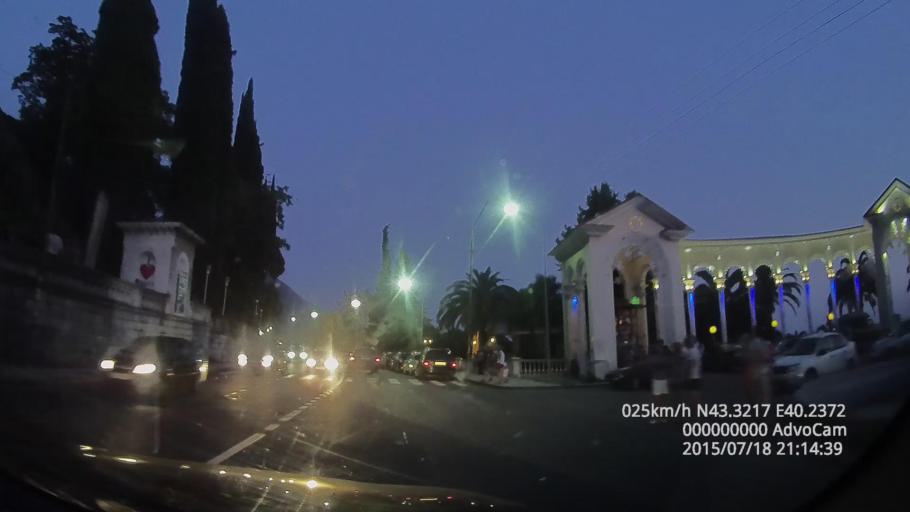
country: GE
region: Abkhazia
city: Gagra
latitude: 43.3215
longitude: 40.2374
